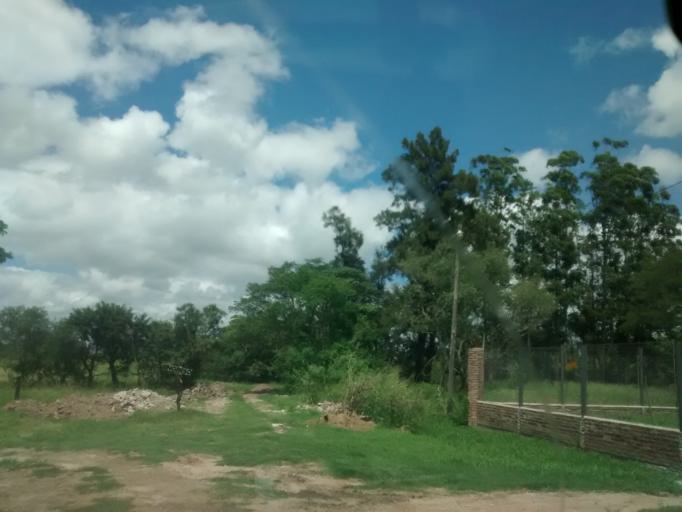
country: AR
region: Chaco
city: Fontana
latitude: -27.4116
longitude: -58.9820
